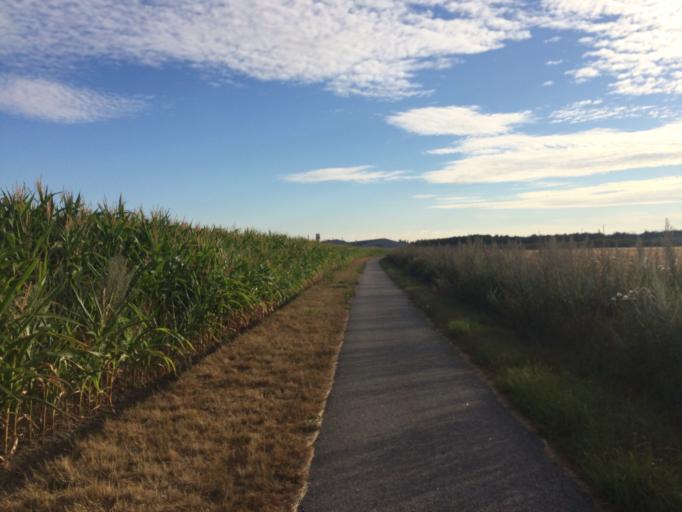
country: DK
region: Central Jutland
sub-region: Holstebro Kommune
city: Vinderup
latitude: 56.6089
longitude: 8.8699
